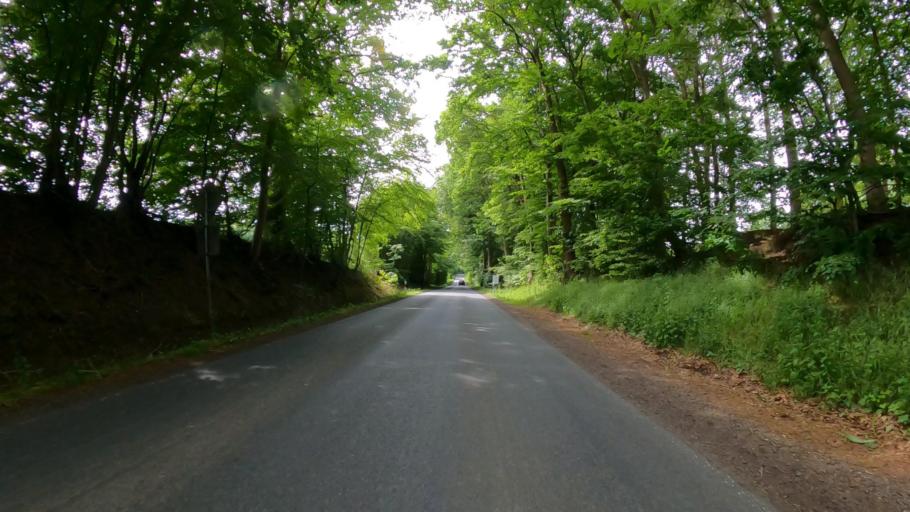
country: DE
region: Schleswig-Holstein
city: Huttblek
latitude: 53.8089
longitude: 10.0912
